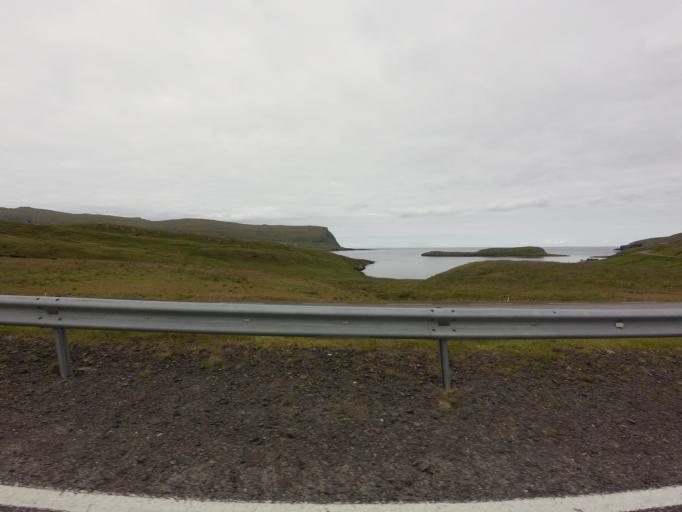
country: FO
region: Suduroy
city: Tvoroyri
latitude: 61.5298
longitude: -6.7958
